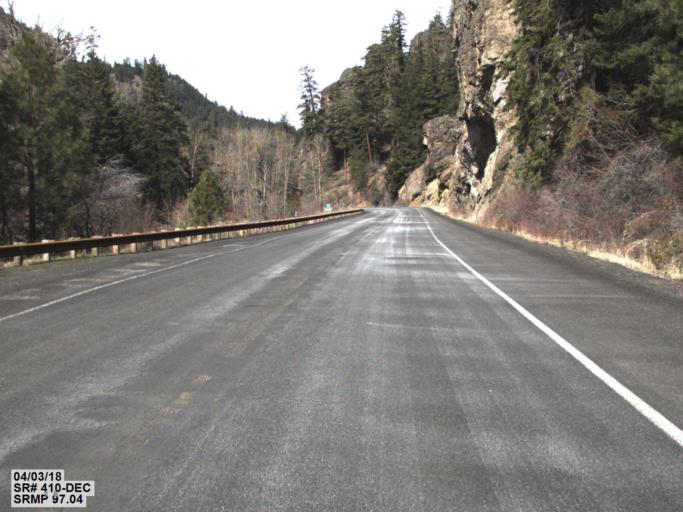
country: US
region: Washington
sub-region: Kittitas County
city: Cle Elum
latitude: 46.9317
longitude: -121.0525
